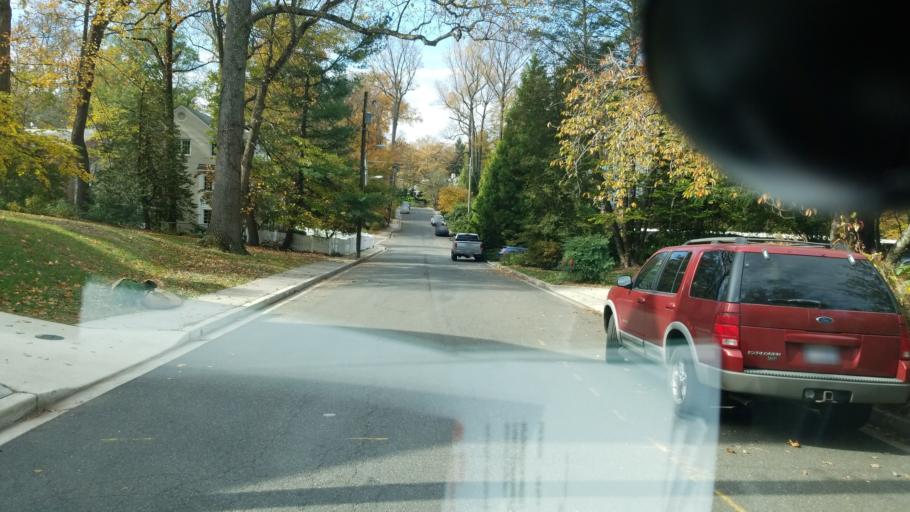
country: US
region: Maryland
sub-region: Montgomery County
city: Chevy Chase
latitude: 38.9772
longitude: -77.0563
